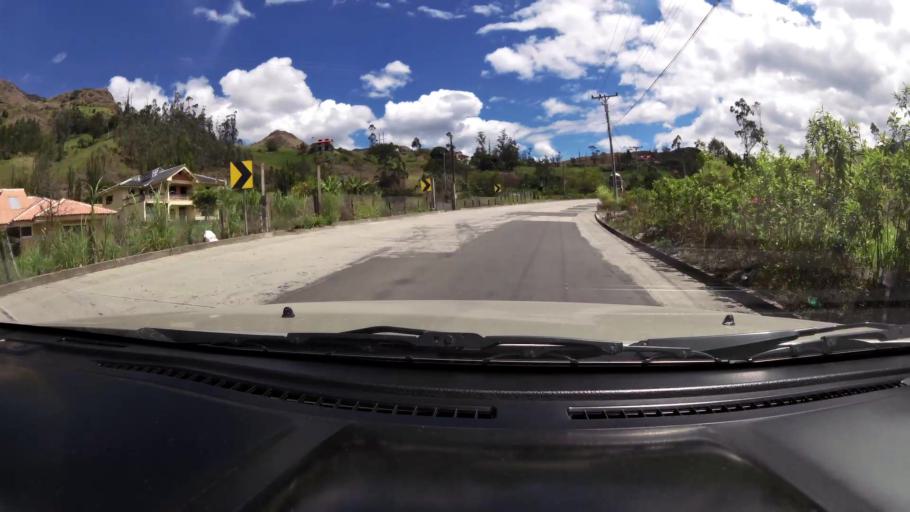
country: EC
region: Azuay
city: Cuenca
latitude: -3.1782
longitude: -79.1672
